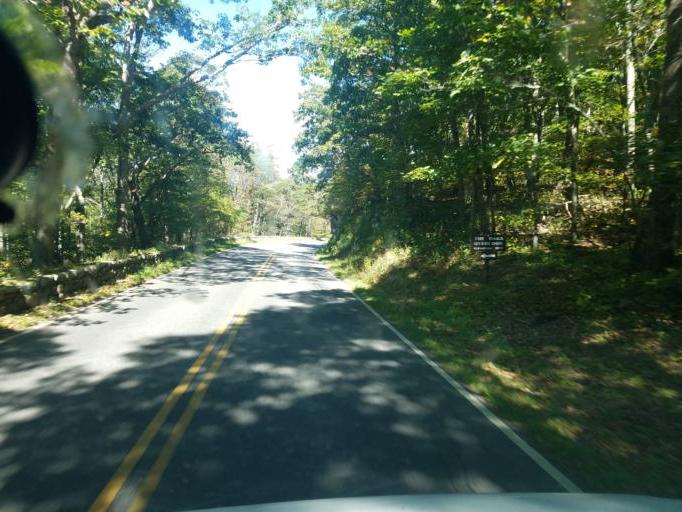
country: US
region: Virginia
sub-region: Greene County
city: Stanardsville
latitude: 38.4182
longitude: -78.4878
